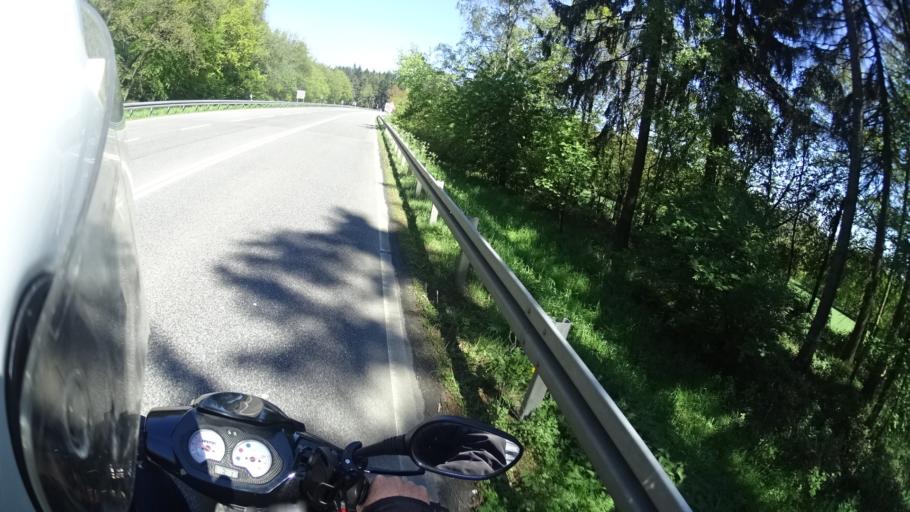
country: DE
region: Hesse
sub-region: Regierungsbezirk Darmstadt
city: Bad Schwalbach
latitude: 50.1173
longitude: 8.0777
